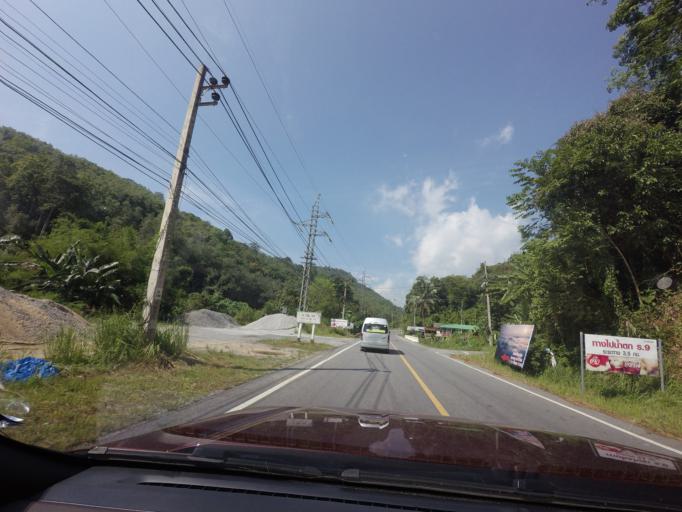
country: TH
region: Yala
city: Betong
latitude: 5.9438
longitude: 101.1897
